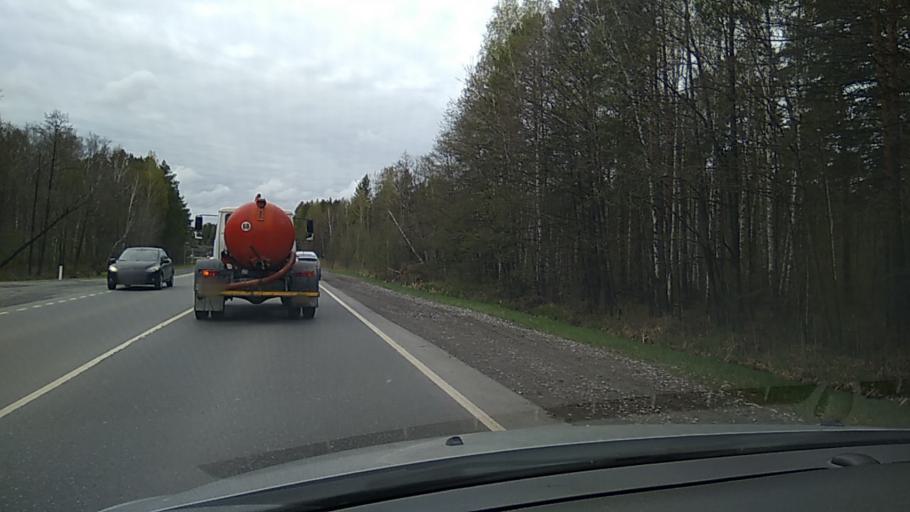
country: RU
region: Tjumen
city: Chervishevo
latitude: 56.9719
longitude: 65.4399
